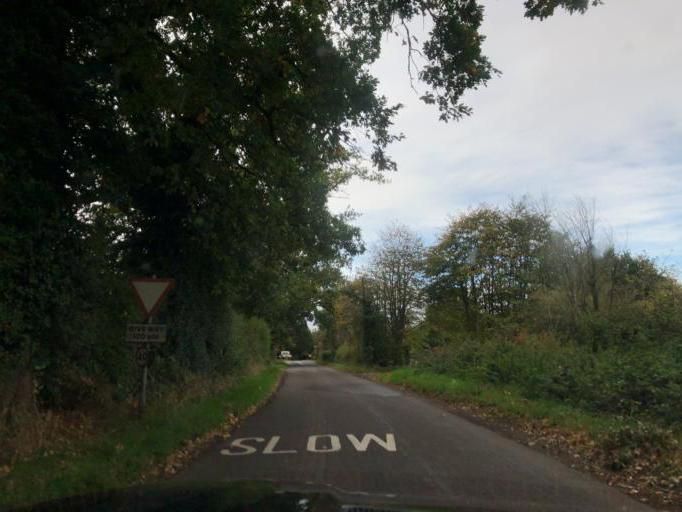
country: GB
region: England
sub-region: Warwickshire
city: Wroxall
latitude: 52.3368
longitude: -1.6563
